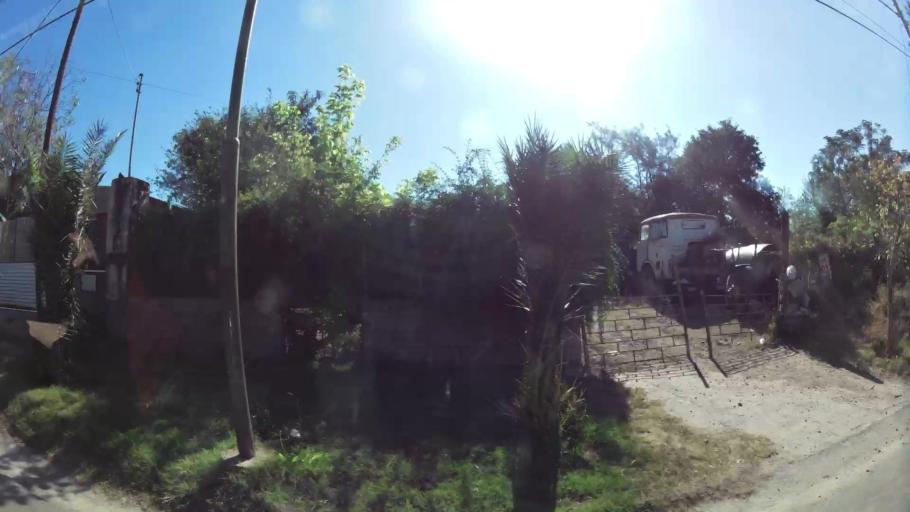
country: AR
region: Cordoba
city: La Calera
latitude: -31.3560
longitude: -64.3142
